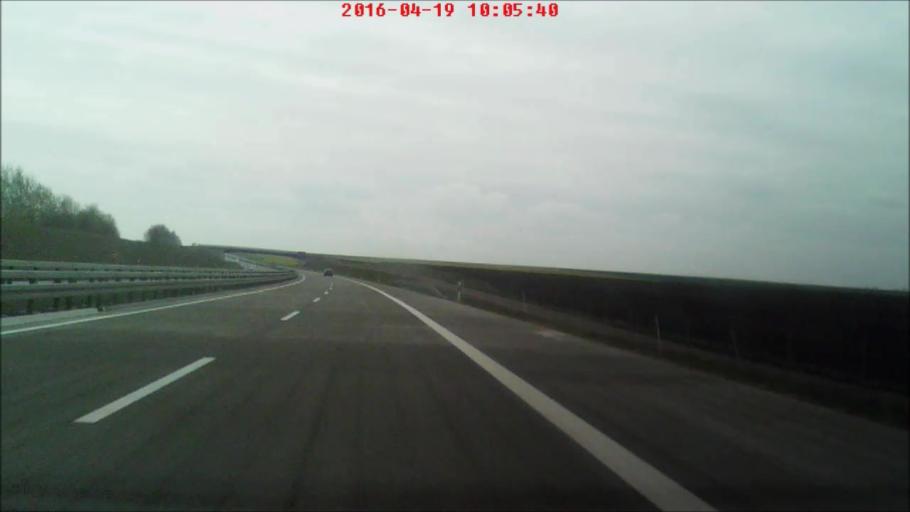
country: DE
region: Thuringia
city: Schillingstedt
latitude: 51.2211
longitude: 11.1840
